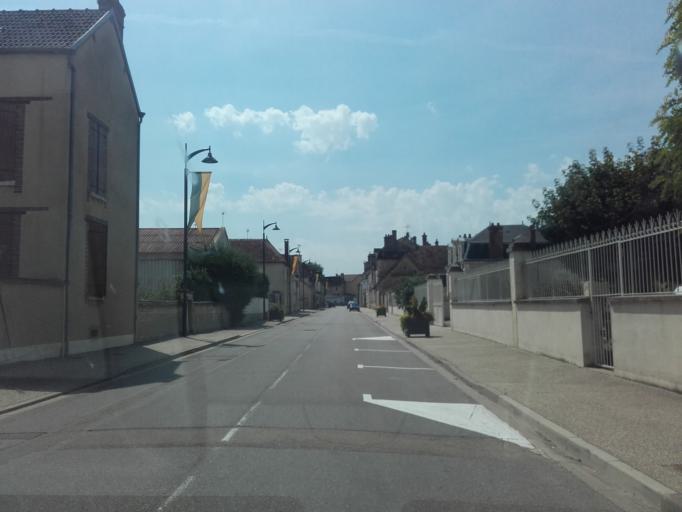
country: FR
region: Bourgogne
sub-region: Departement de l'Yonne
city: Chablis
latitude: 47.8164
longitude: 3.8055
